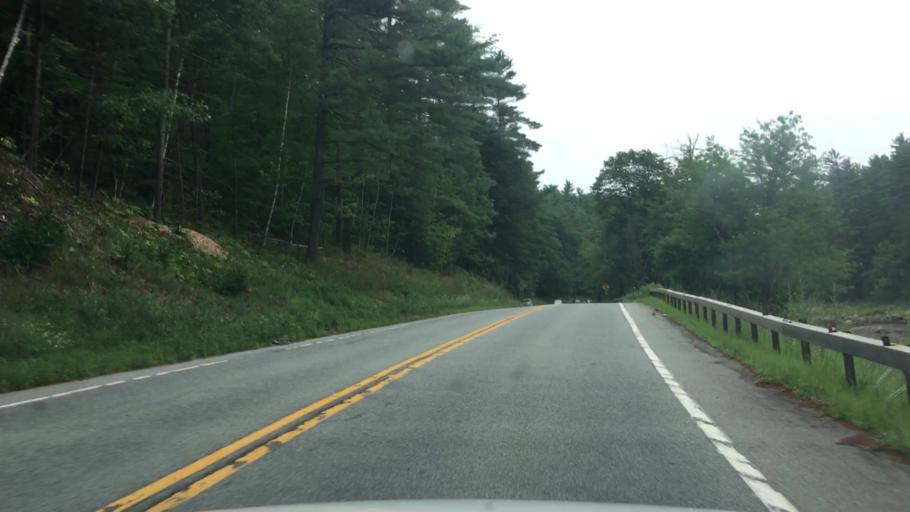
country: US
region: New York
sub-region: Essex County
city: Keeseville
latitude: 44.4204
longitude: -73.6816
